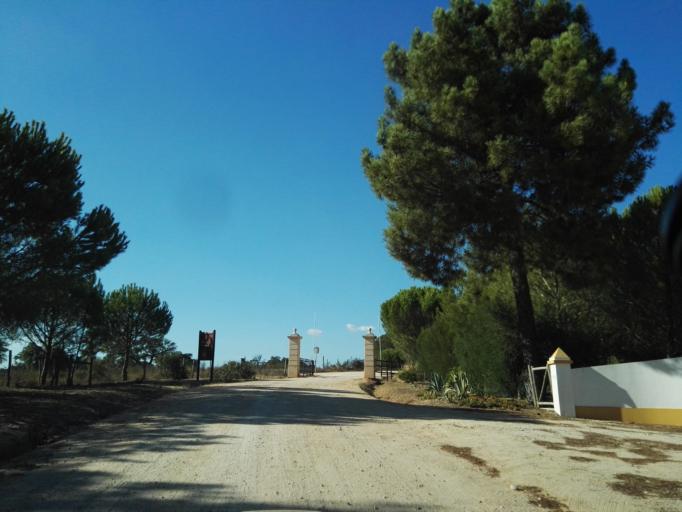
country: PT
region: Santarem
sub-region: Benavente
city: Poceirao
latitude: 38.8774
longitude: -8.7407
